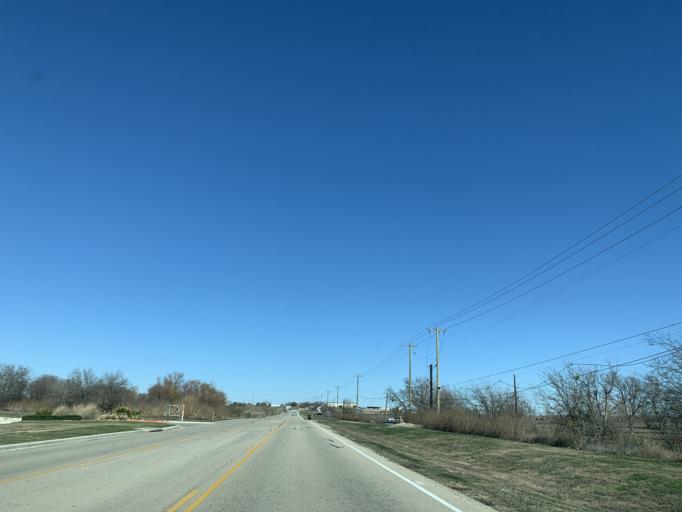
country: US
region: Texas
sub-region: Williamson County
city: Hutto
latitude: 30.5544
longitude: -97.5716
